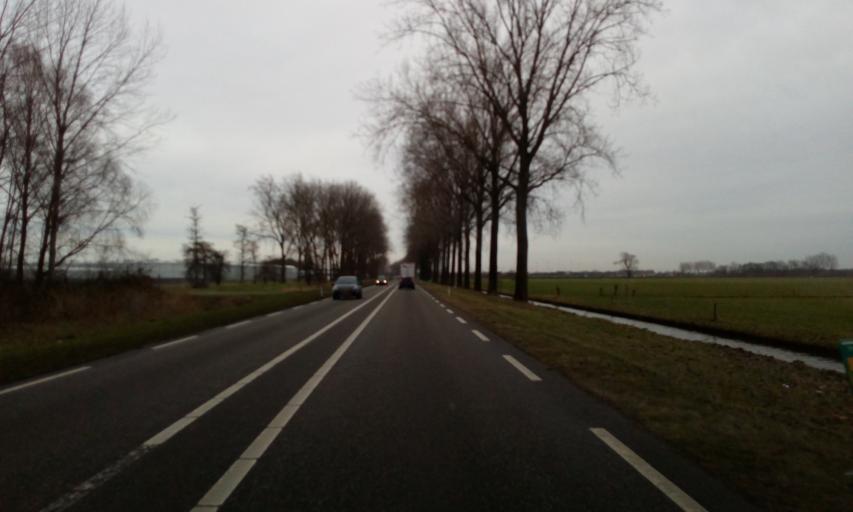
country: NL
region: Gelderland
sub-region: Gemeente Zaltbommel
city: Zaltbommel
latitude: 51.7971
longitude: 5.2257
